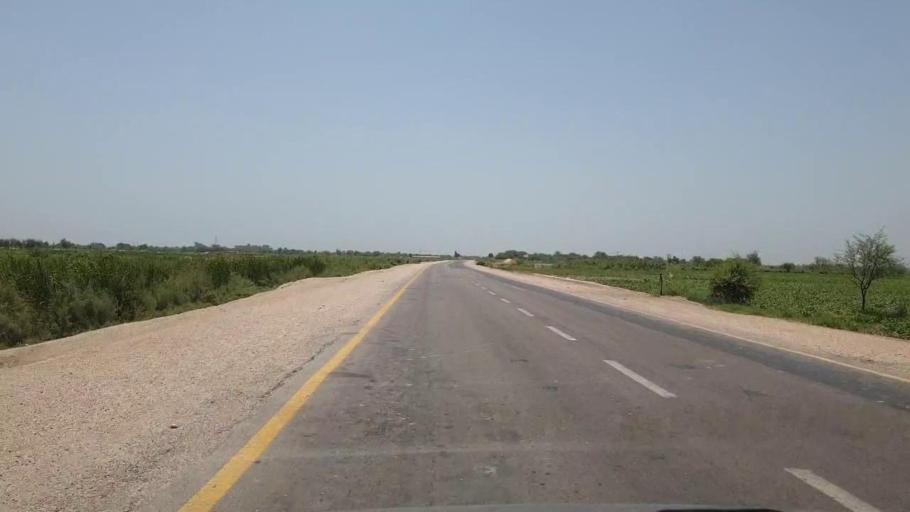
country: PK
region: Sindh
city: Sakrand
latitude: 26.1272
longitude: 68.3794
